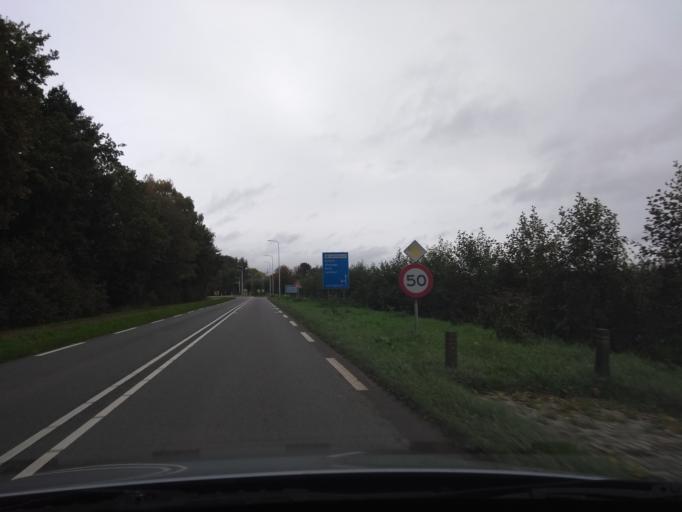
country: NL
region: Overijssel
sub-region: Gemeente Steenwijkerland
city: Blokzijl
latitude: 52.7406
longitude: 5.8573
